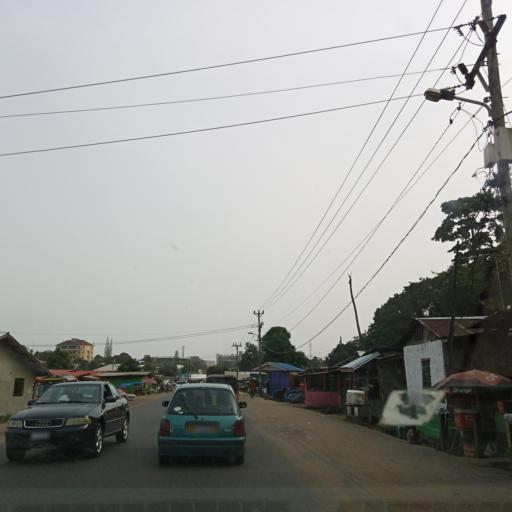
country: LR
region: Montserrado
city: Monrovia
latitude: 6.2997
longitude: -10.7929
